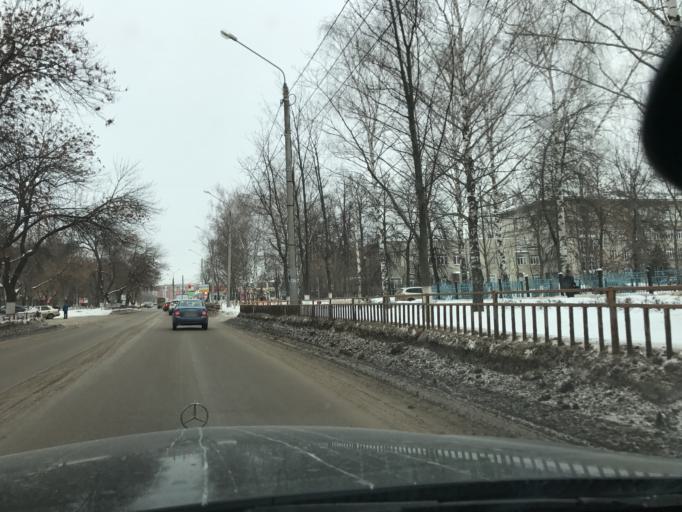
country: RU
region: Nizjnij Novgorod
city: Gorbatovka
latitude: 56.2483
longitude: 43.8512
